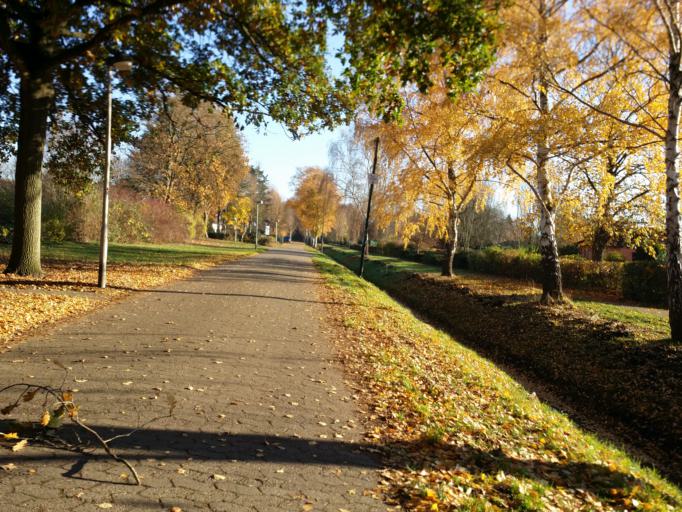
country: DE
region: Lower Saxony
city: Lilienthal
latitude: 53.0683
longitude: 8.8957
